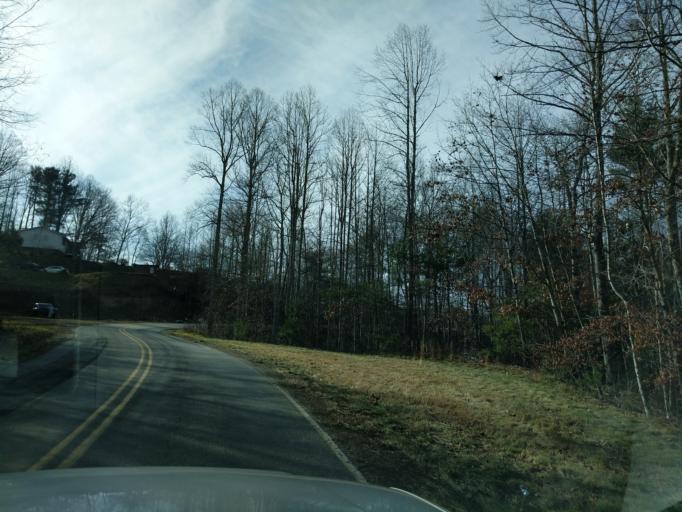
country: US
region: North Carolina
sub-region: Haywood County
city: Cove Creek
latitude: 35.6673
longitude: -83.0150
